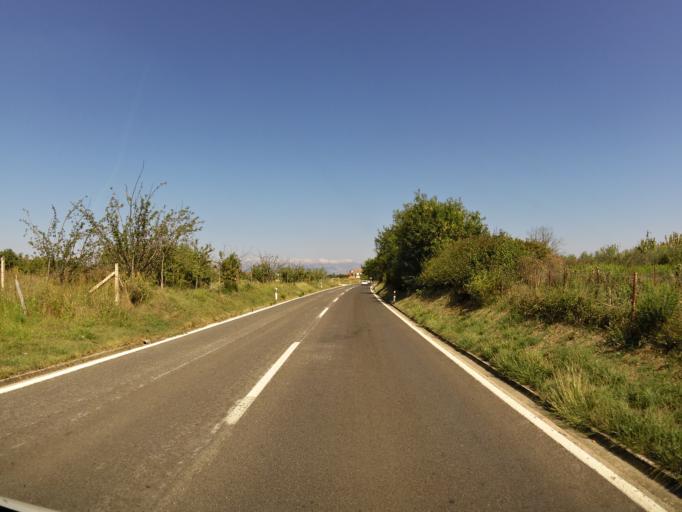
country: HR
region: Zadarska
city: Policnik
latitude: 44.1561
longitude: 15.3384
